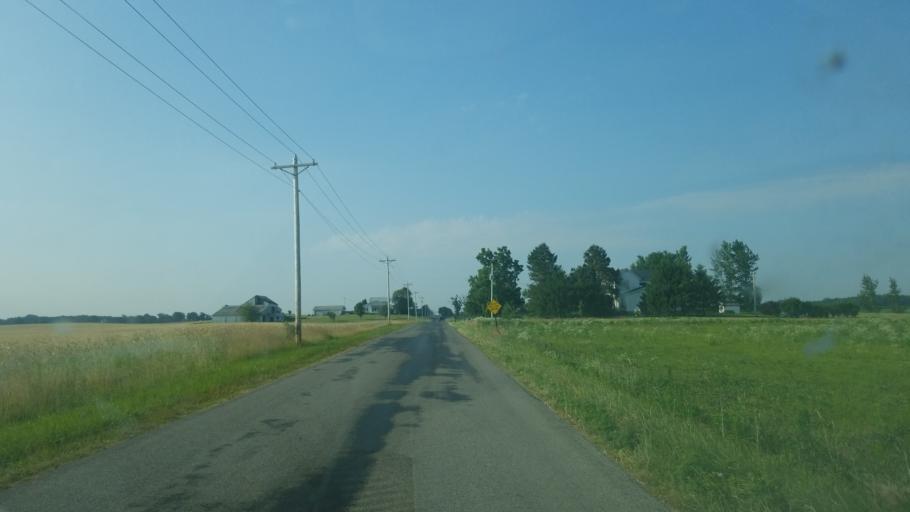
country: US
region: Ohio
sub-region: Hardin County
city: Kenton
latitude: 40.6189
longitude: -83.7199
